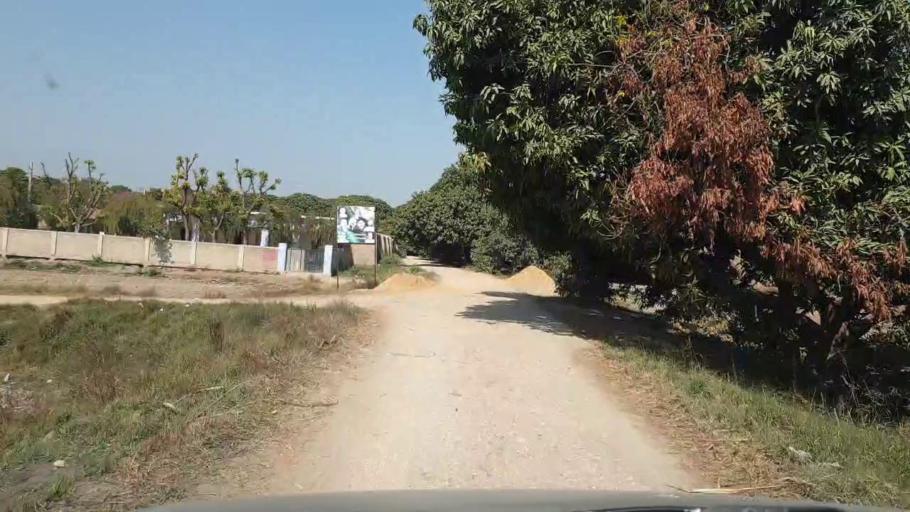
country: PK
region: Sindh
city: Tando Jam
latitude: 25.4020
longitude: 68.6310
